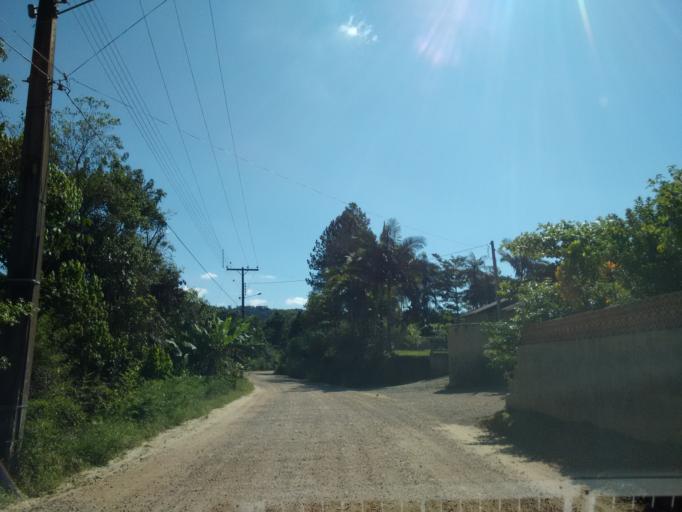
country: BR
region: Santa Catarina
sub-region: Indaial
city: Indaial
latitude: -26.8979
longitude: -49.1898
